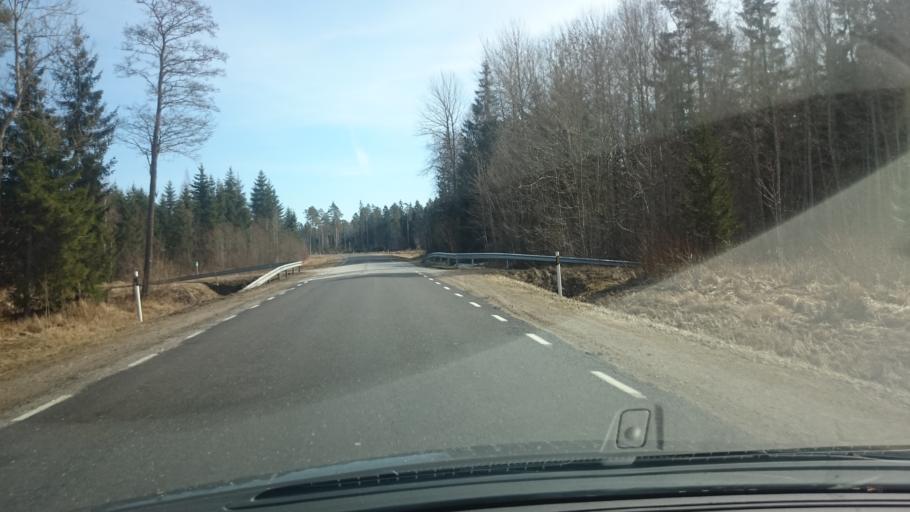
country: EE
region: Paernumaa
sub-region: Tootsi vald
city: Tootsi
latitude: 58.6422
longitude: 24.8885
